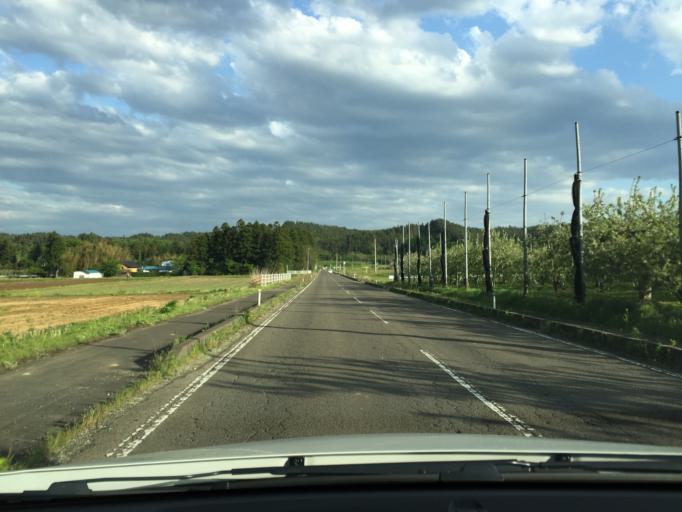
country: JP
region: Fukushima
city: Fukushima-shi
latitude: 37.7221
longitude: 140.3912
